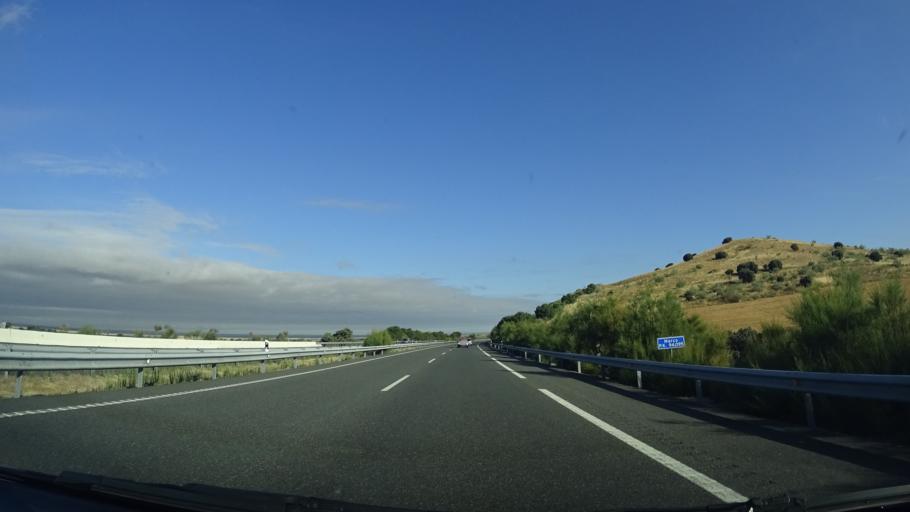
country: ES
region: Castille and Leon
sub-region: Provincia de Segovia
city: Labajos
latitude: 40.8386
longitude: -4.5338
